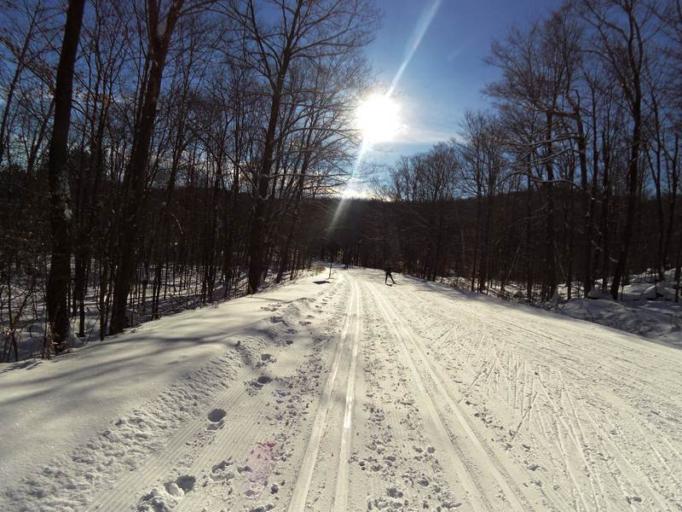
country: CA
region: Quebec
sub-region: Outaouais
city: Wakefield
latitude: 45.5199
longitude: -75.8544
